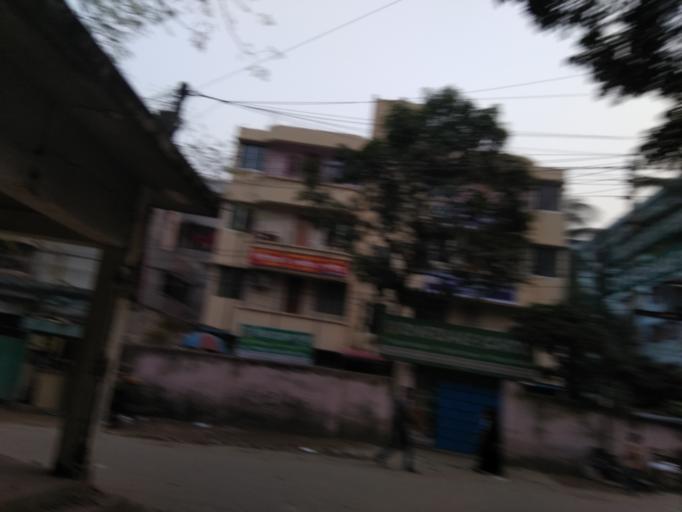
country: BD
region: Dhaka
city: Tungi
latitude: 23.8149
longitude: 90.3681
